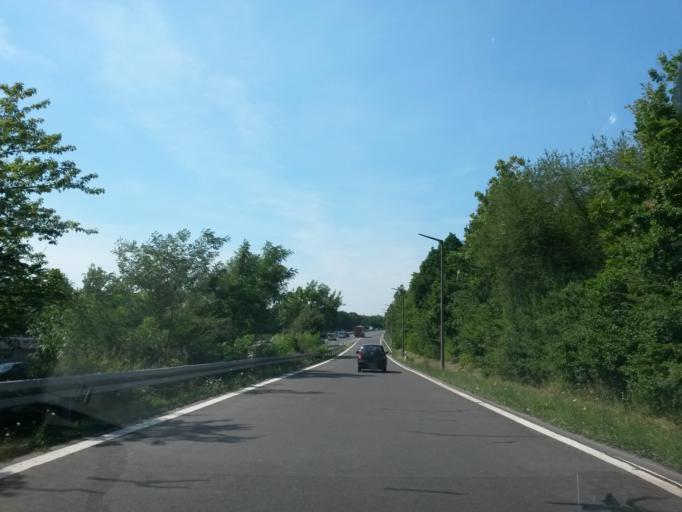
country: DE
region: Bavaria
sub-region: Regierungsbezirk Mittelfranken
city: Zirndorf
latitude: 49.4684
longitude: 10.9551
